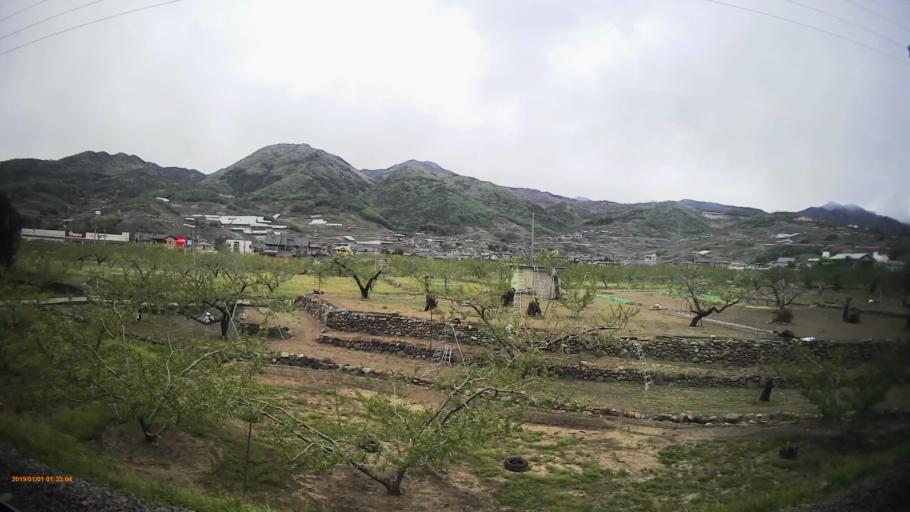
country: JP
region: Yamanashi
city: Isawa
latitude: 35.6786
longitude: 138.6653
